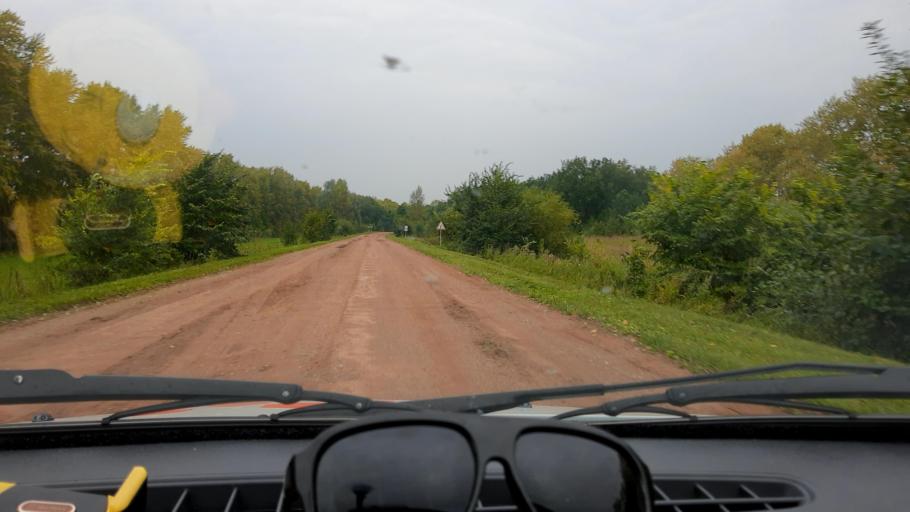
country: RU
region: Bashkortostan
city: Asanovo
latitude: 54.9924
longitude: 55.6966
